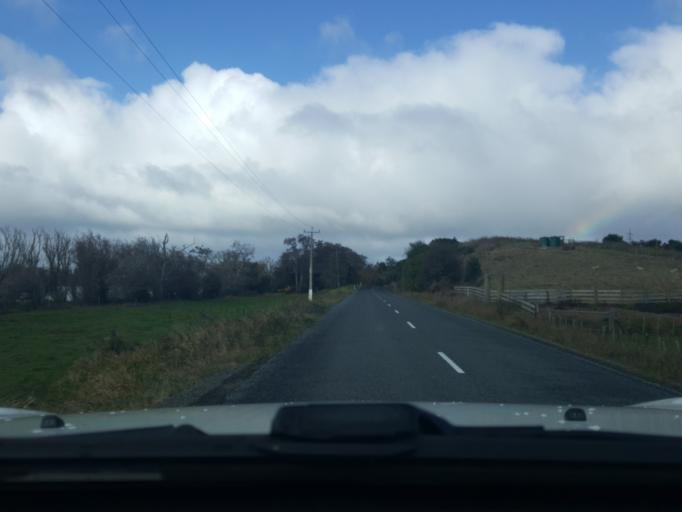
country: NZ
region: Waikato
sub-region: Waikato District
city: Te Kauwhata
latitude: -37.4004
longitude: 175.0591
